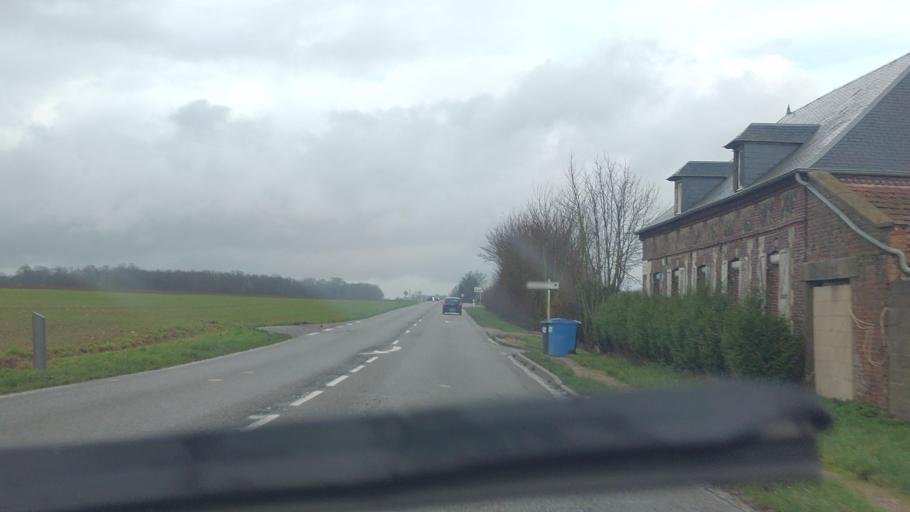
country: FR
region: Picardie
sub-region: Departement de l'Oise
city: Milly-sur-Therain
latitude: 49.5086
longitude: 2.0164
